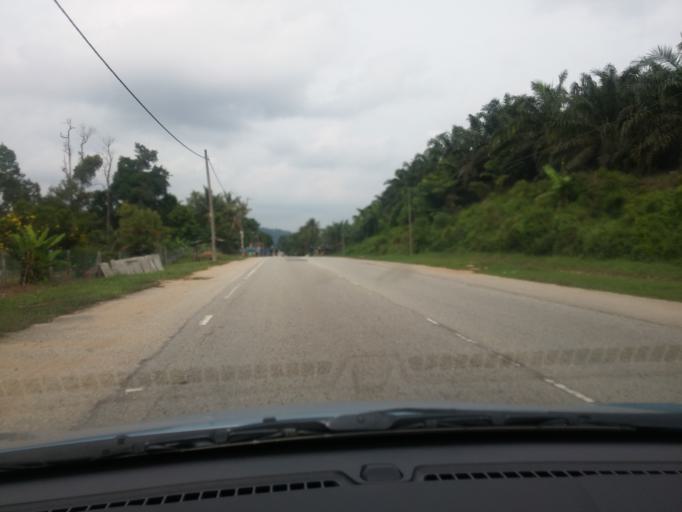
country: MY
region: Pahang
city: Kuantan
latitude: 3.8820
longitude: 103.1691
